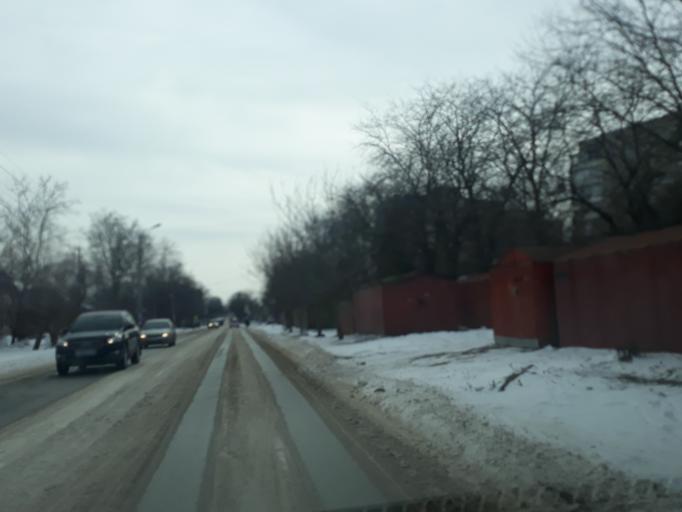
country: RU
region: Rostov
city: Taganrog
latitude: 47.2274
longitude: 38.8762
